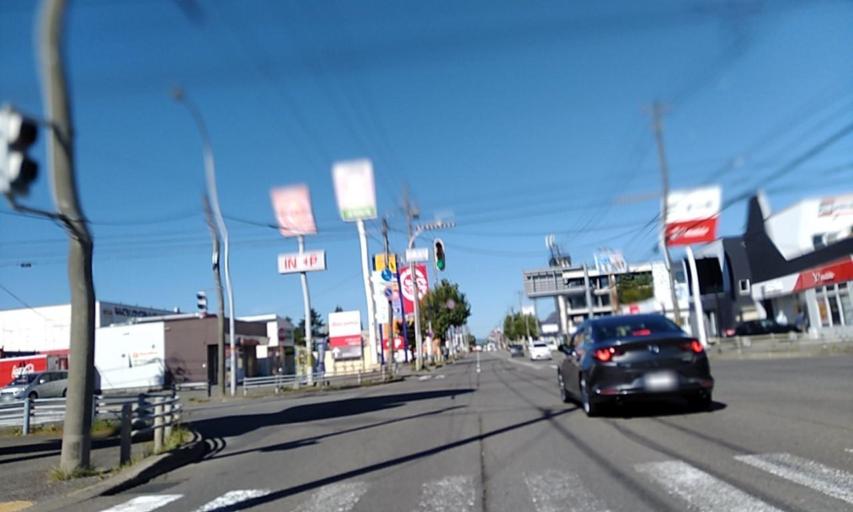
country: JP
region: Hokkaido
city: Chitose
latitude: 42.8379
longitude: 141.6380
